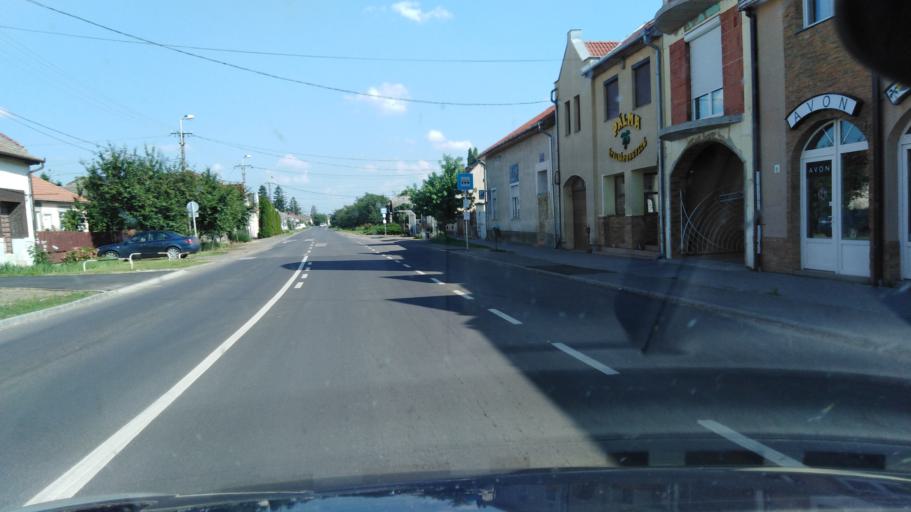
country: HU
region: Szabolcs-Szatmar-Bereg
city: Nyirbator
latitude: 47.8331
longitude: 22.1348
